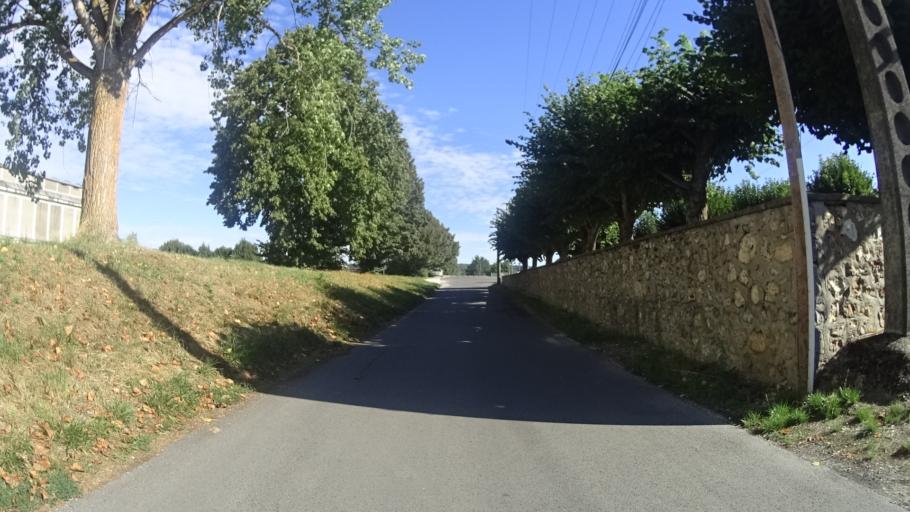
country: FR
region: Centre
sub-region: Departement du Cher
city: Saint-Satur
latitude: 47.3376
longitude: 2.8593
